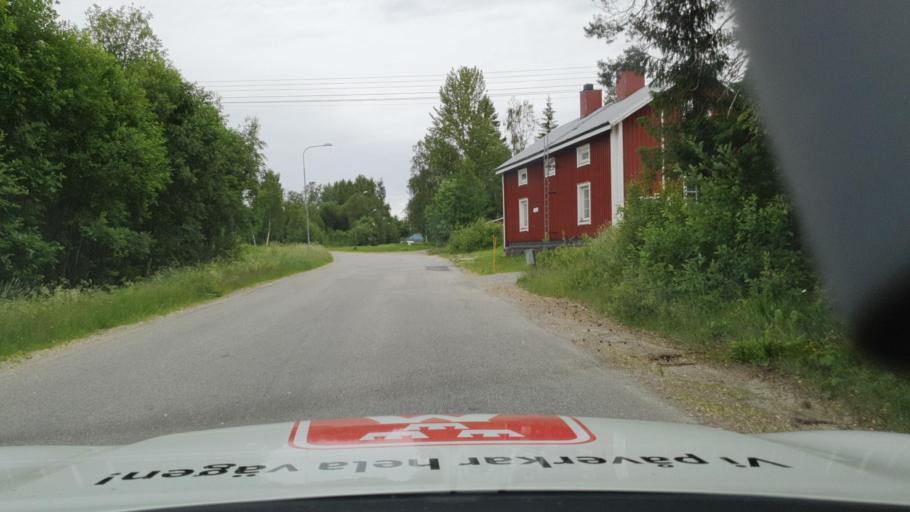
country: SE
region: Vaesterbotten
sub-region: Nordmalings Kommun
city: Nordmaling
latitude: 63.5361
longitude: 19.4433
